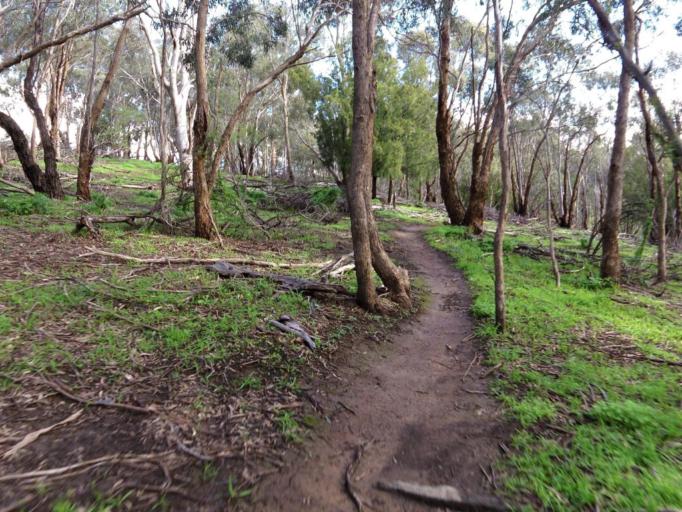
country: AU
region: Victoria
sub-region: Banyule
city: Watsonia North
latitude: -37.6826
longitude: 145.0821
